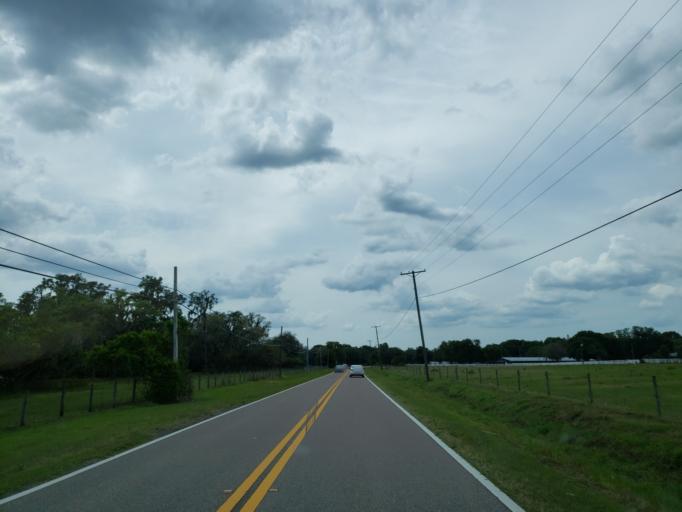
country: US
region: Florida
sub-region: Hillsborough County
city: Citrus Park
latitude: 28.1087
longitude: -82.6002
